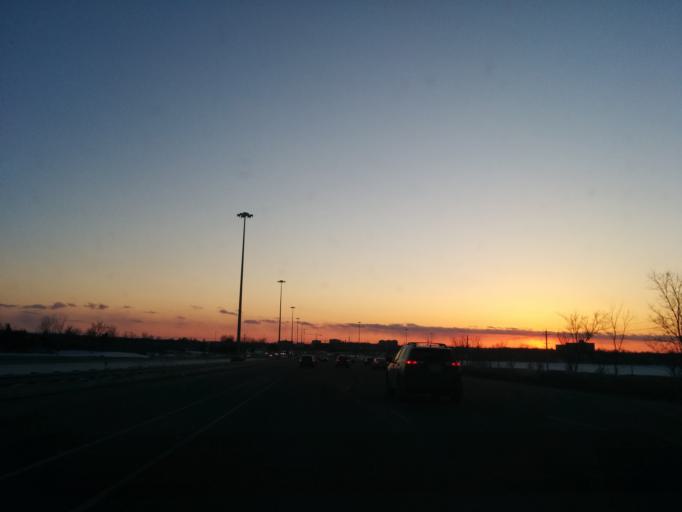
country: CA
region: Ontario
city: Bells Corners
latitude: 45.3250
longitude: -75.8749
